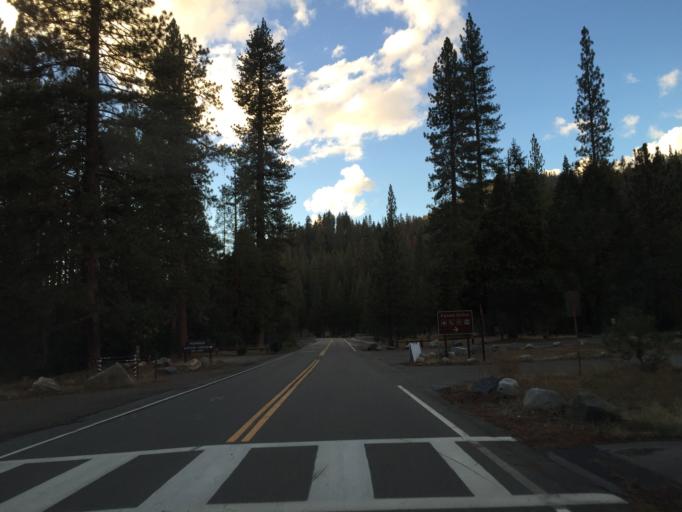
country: US
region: California
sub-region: Madera County
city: Ahwahnee
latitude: 37.5374
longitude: -119.6581
